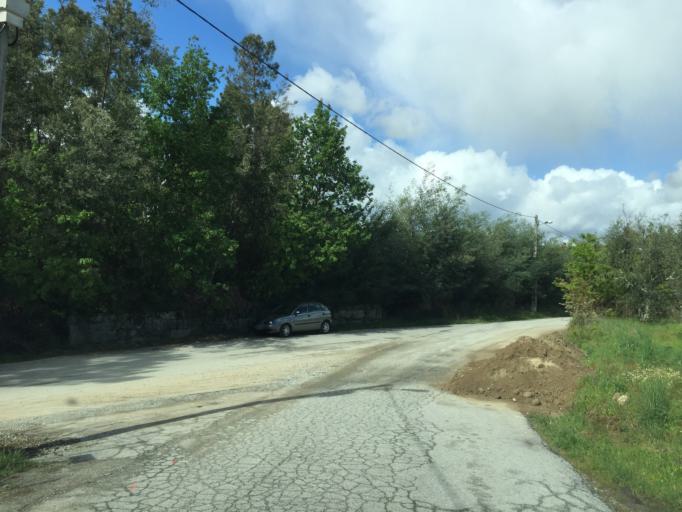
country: PT
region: Viseu
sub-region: Viseu
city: Abraveses
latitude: 40.6598
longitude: -7.9461
